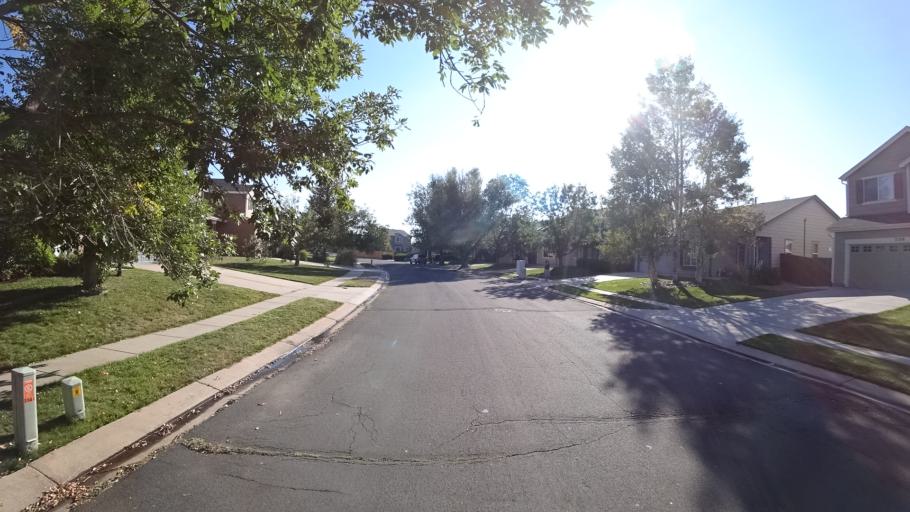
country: US
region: Colorado
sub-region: El Paso County
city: Cimarron Hills
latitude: 38.8814
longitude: -104.6942
